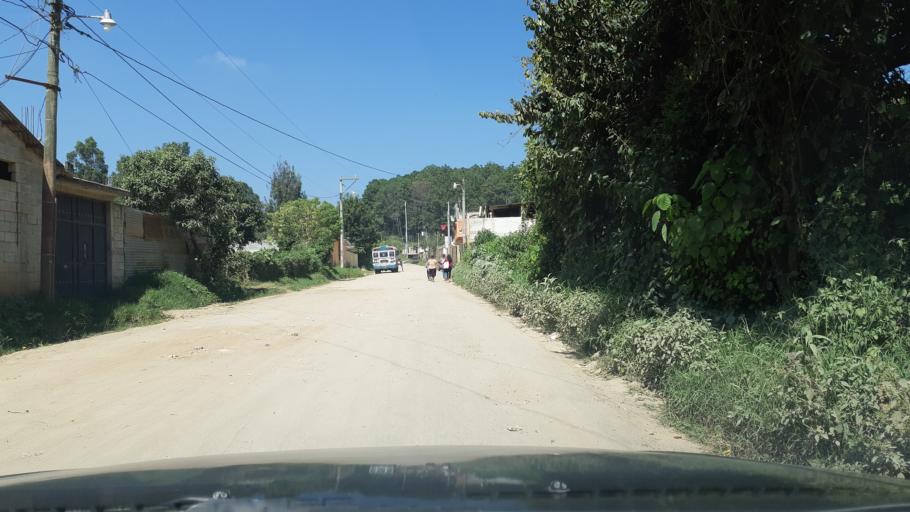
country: GT
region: Chimaltenango
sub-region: Municipio de Chimaltenango
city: Chimaltenango
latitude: 14.6692
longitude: -90.8372
